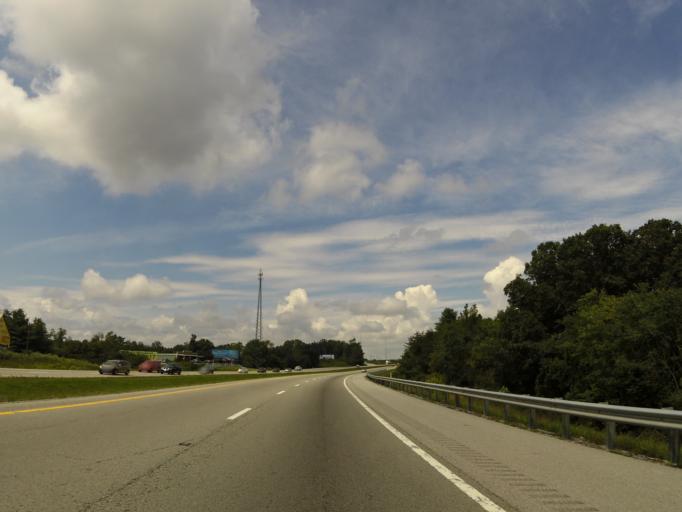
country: US
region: Tennessee
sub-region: Cumberland County
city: Crossville
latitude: 35.9585
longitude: -84.9757
